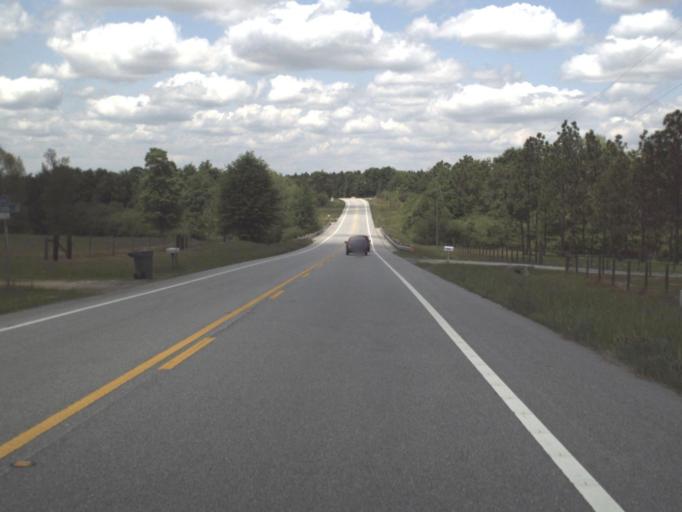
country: US
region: Florida
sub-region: Escambia County
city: Molino
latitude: 30.8082
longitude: -87.4249
